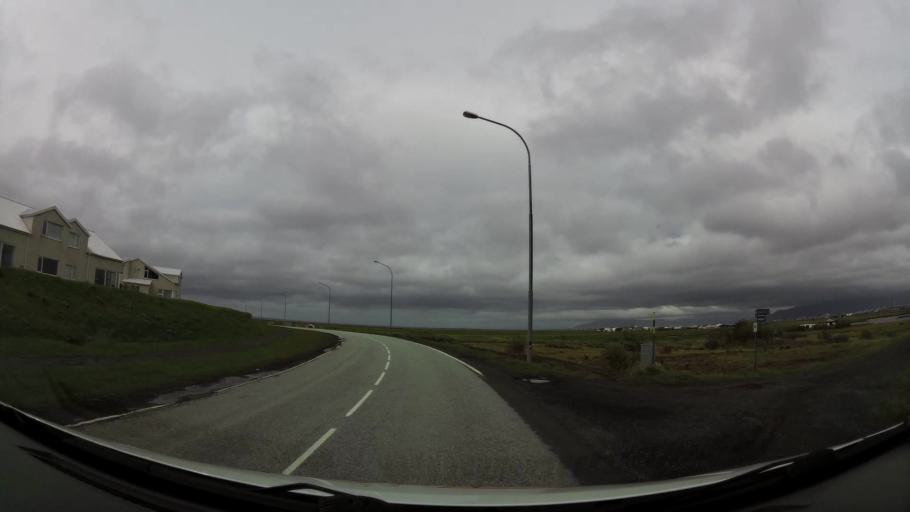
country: IS
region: Capital Region
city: Alftanes
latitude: 64.1077
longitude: -22.0098
